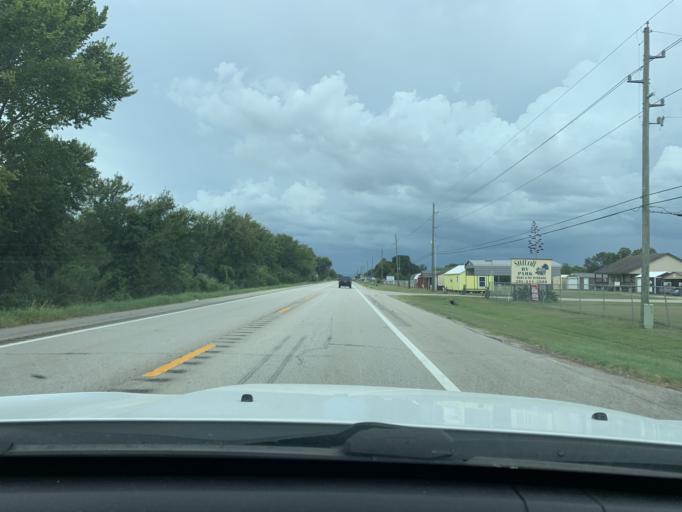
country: US
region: Texas
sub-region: Fort Bend County
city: Greatwood
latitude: 29.5396
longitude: -95.7178
